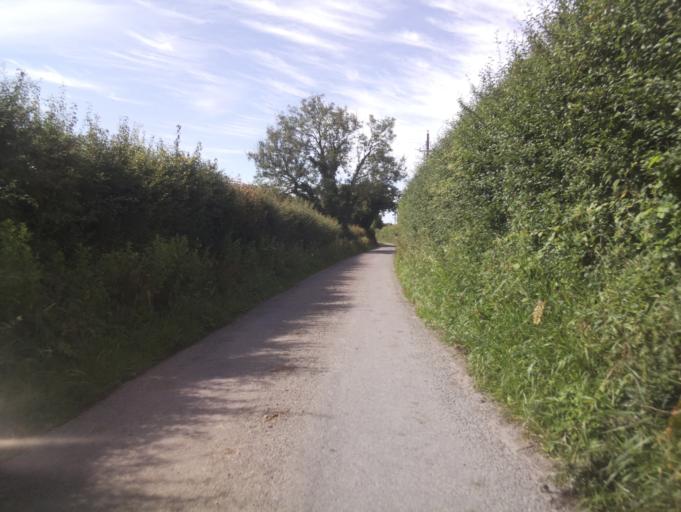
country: GB
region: England
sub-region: South Gloucestershire
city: Horton
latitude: 51.5373
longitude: -2.3612
